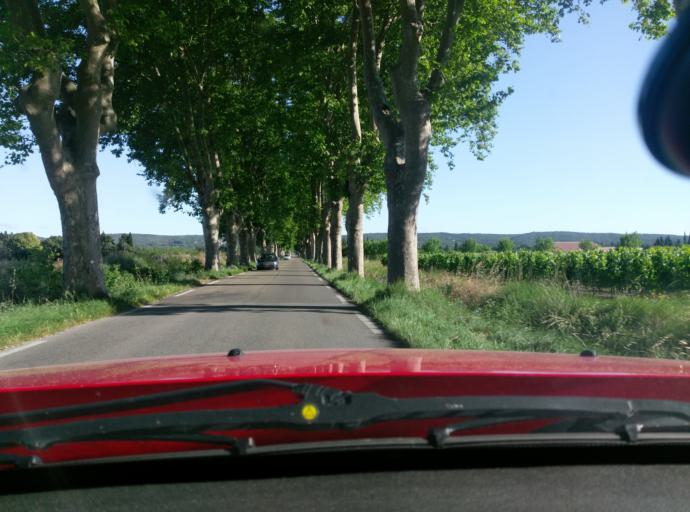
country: FR
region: Languedoc-Roussillon
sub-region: Departement du Gard
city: Uzes
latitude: 44.0383
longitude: 4.4083
